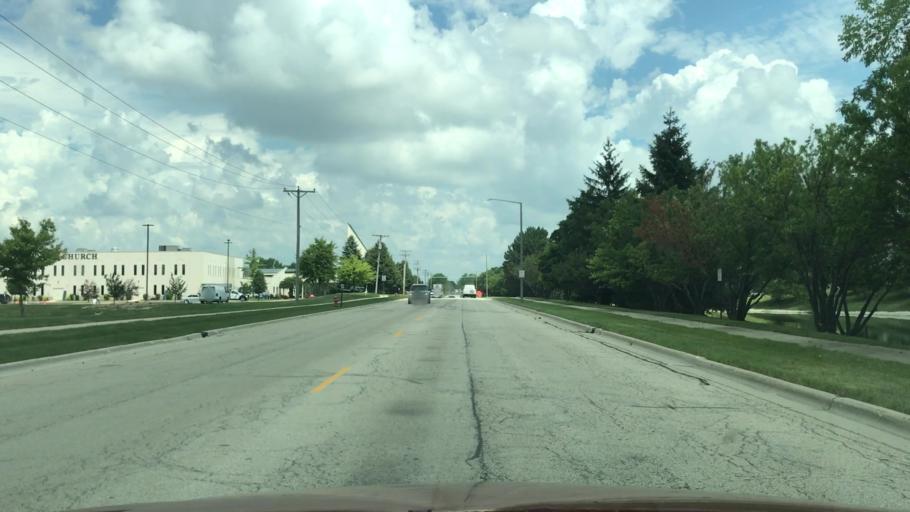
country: US
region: Illinois
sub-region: DuPage County
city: Hanover Park
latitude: 41.9788
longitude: -88.1298
